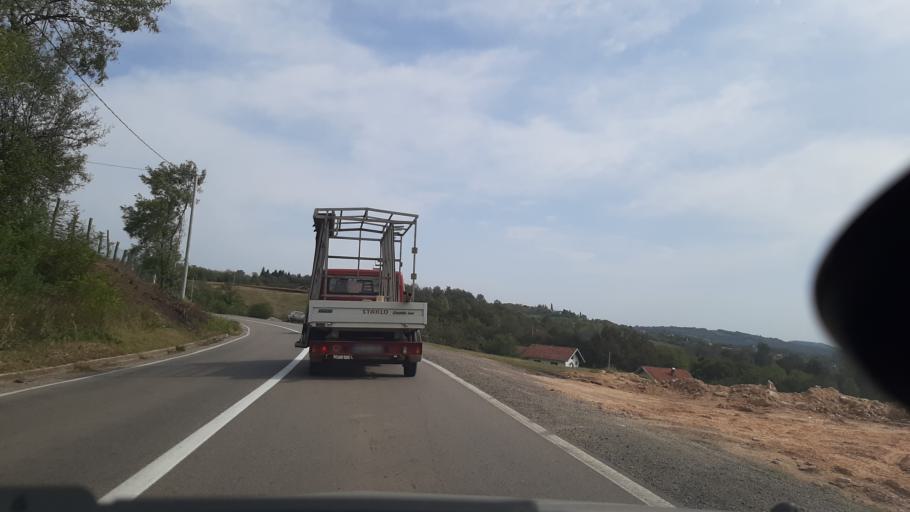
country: BA
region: Republika Srpska
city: Laktasi
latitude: 44.8671
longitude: 17.3440
